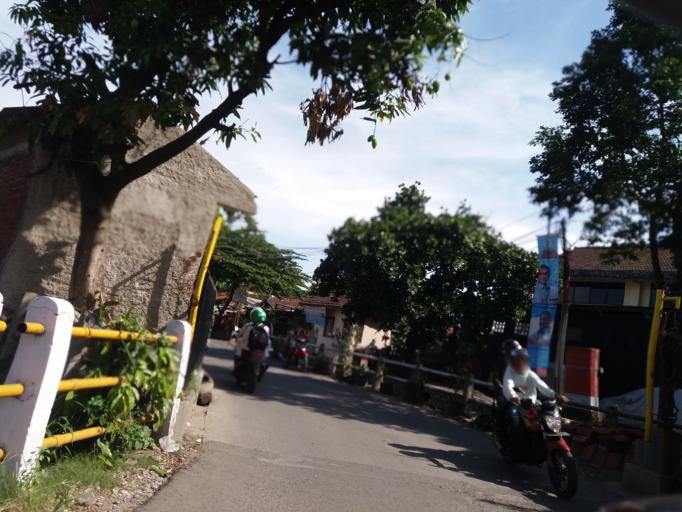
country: ID
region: West Java
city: Bandung
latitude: -6.9445
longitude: 107.6026
